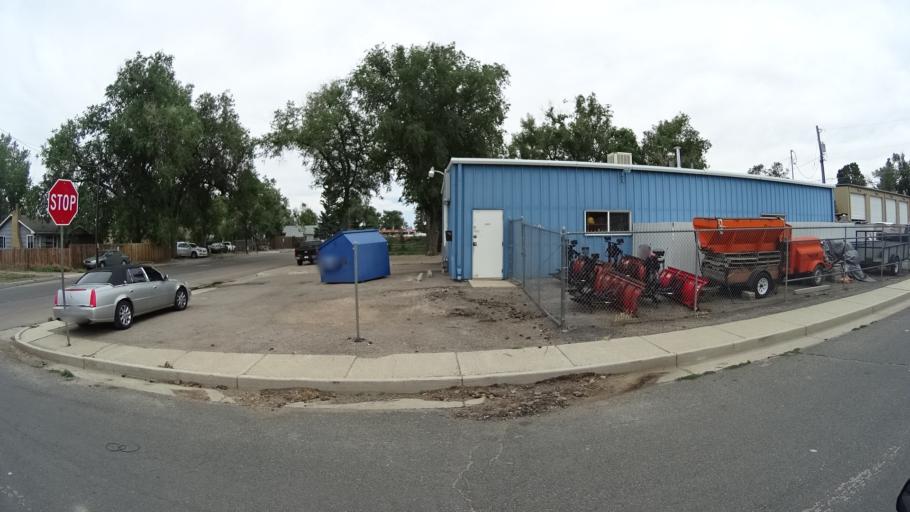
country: US
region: Colorado
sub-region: El Paso County
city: Colorado Springs
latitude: 38.8380
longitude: -104.7792
